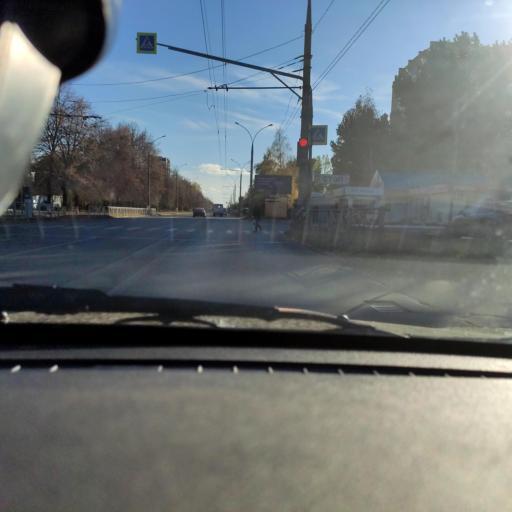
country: RU
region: Samara
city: Tol'yatti
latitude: 53.5365
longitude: 49.2780
